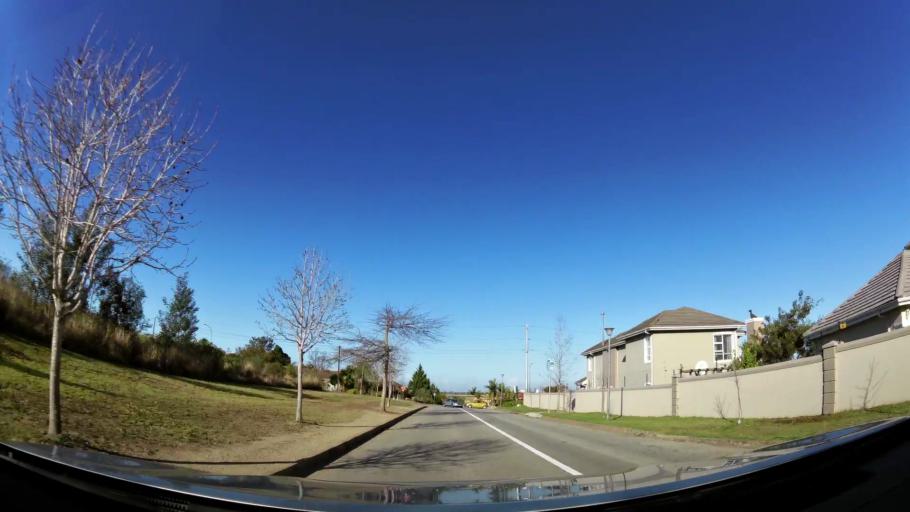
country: ZA
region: Western Cape
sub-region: Eden District Municipality
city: George
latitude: -33.9669
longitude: 22.4382
